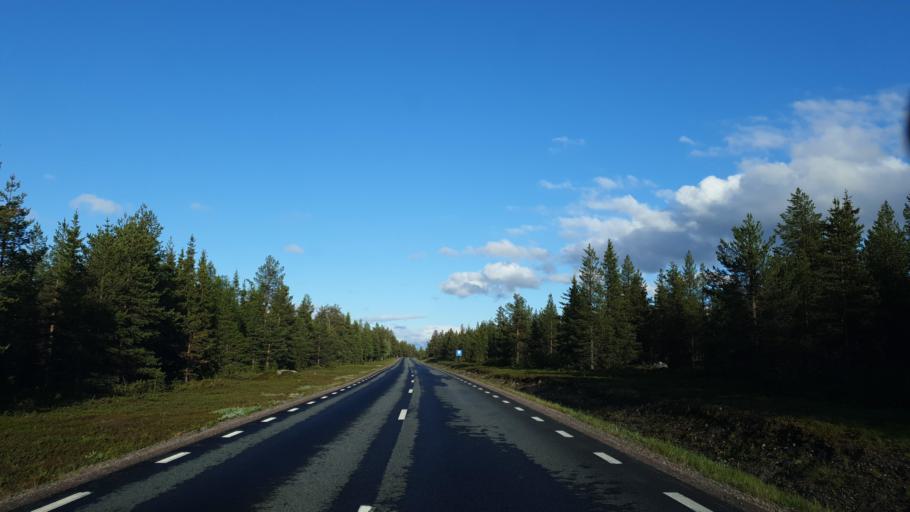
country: SE
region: Norrbotten
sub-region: Arjeplogs Kommun
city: Arjeplog
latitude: 65.9117
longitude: 18.3398
